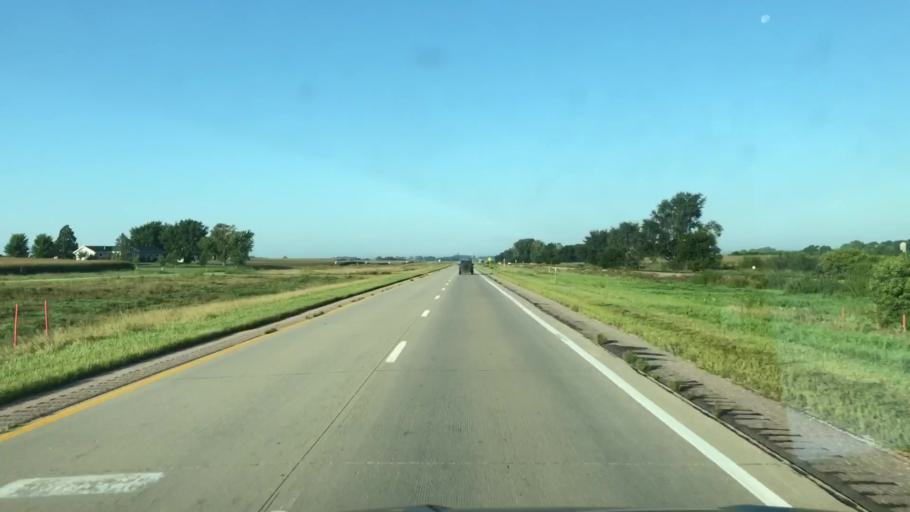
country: US
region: Iowa
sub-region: Sioux County
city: Alton
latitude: 43.0283
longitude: -95.9375
